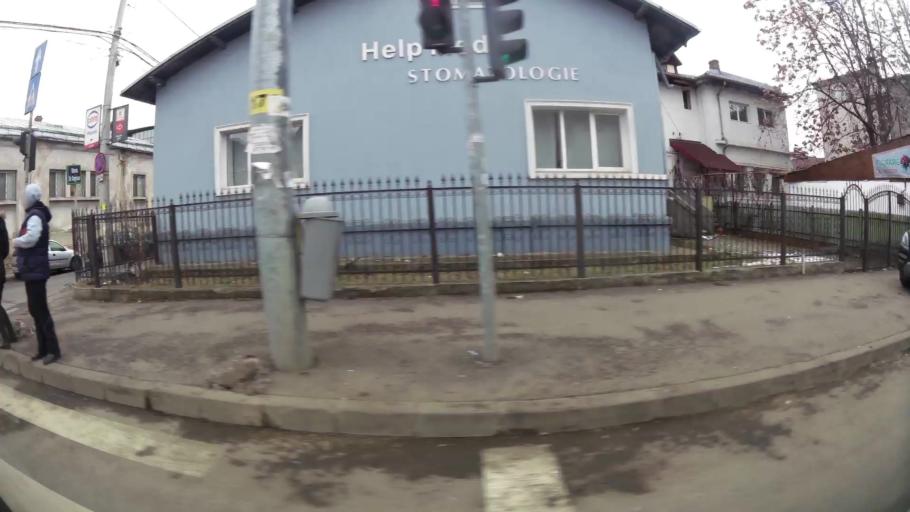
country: RO
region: Prahova
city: Ploiesti
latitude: 44.9391
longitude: 26.0283
